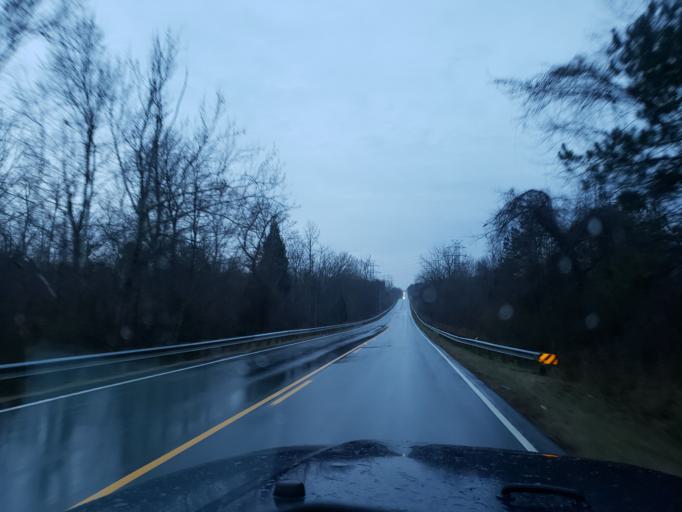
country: US
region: South Carolina
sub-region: Cherokee County
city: Blacksburg
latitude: 35.1438
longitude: -81.4566
